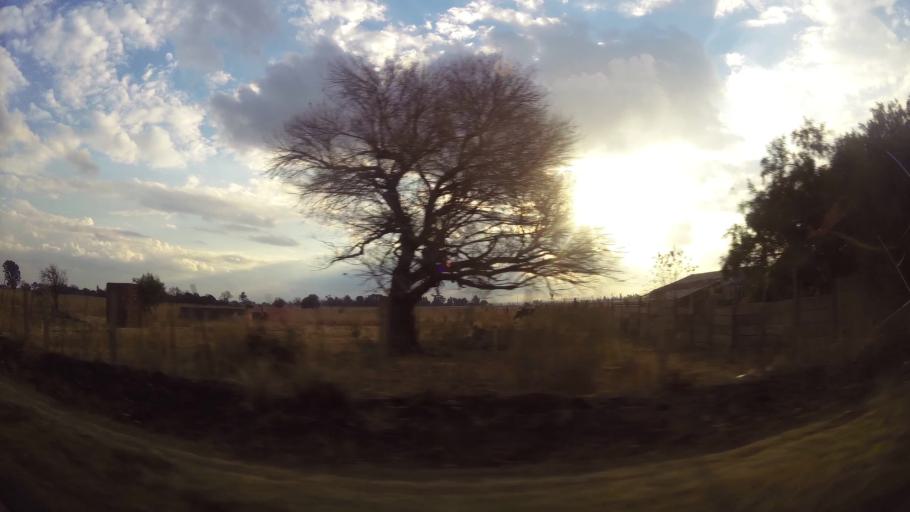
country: ZA
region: Gauteng
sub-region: Sedibeng District Municipality
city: Vanderbijlpark
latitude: -26.6335
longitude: 27.8080
